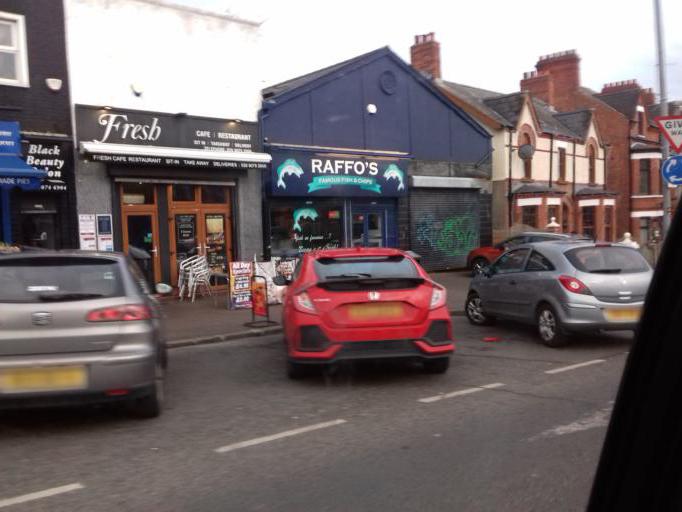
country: GB
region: Northern Ireland
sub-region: City of Belfast
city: Belfast
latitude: 54.6213
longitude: -5.9543
